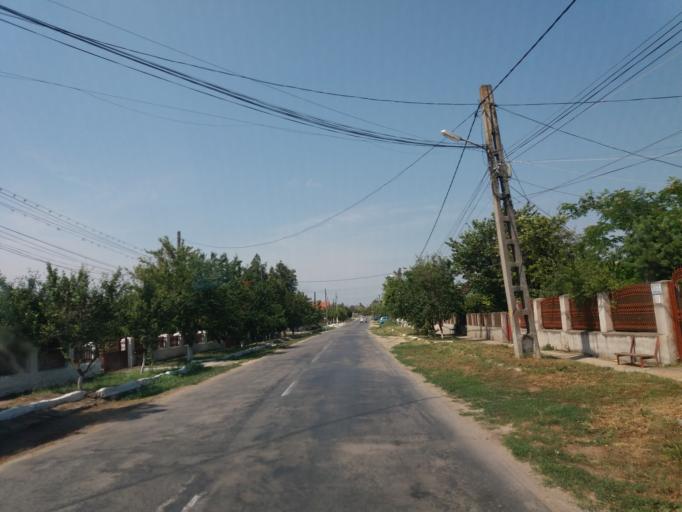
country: RO
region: Constanta
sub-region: Comuna Corbu
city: Corbu
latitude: 44.4160
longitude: 28.6610
